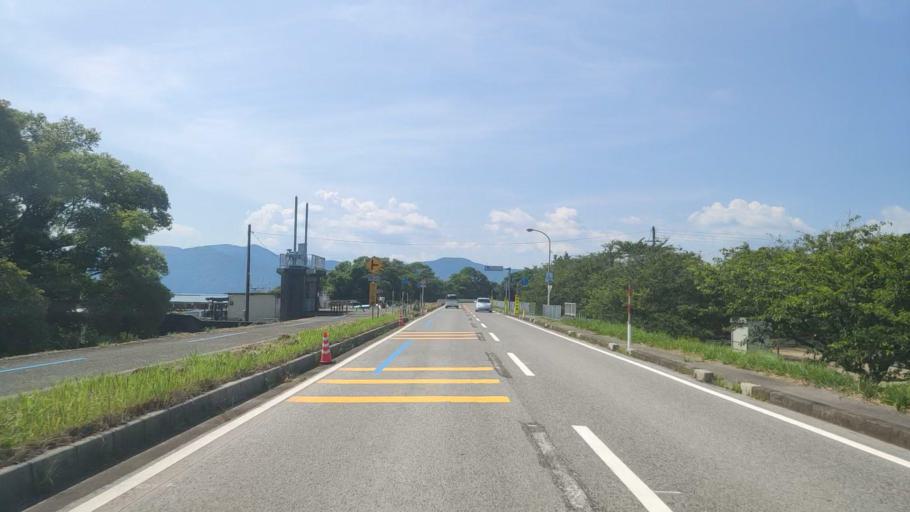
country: JP
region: Shiga Prefecture
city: Nagahama
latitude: 35.4392
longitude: 136.1917
